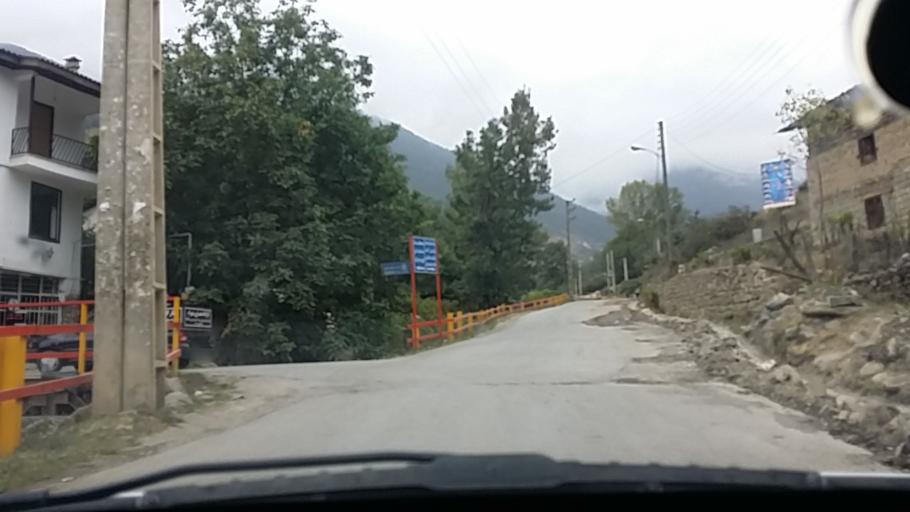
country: IR
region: Mazandaran
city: `Abbasabad
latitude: 36.4825
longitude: 51.1370
